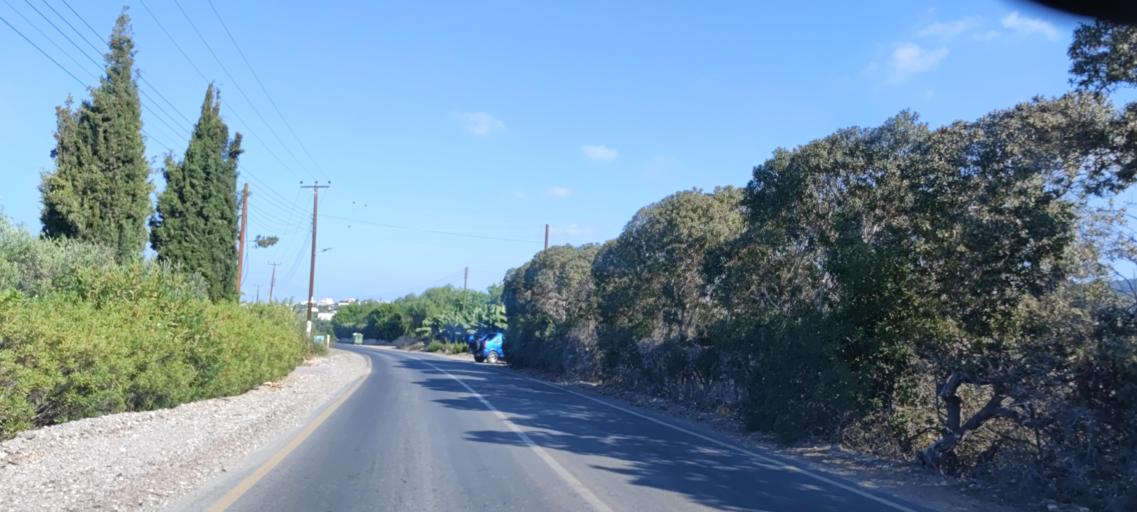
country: CY
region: Pafos
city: Pegeia
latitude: 34.8728
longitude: 32.3464
